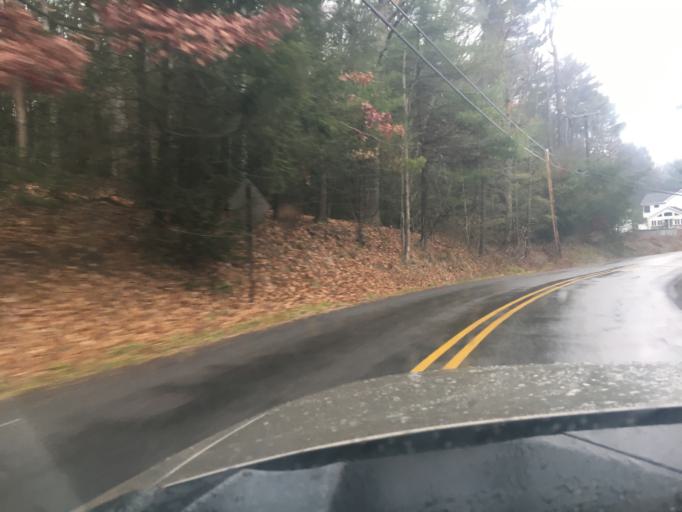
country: US
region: Pennsylvania
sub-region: Luzerne County
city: Harleigh
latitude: 41.0316
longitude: -75.9853
